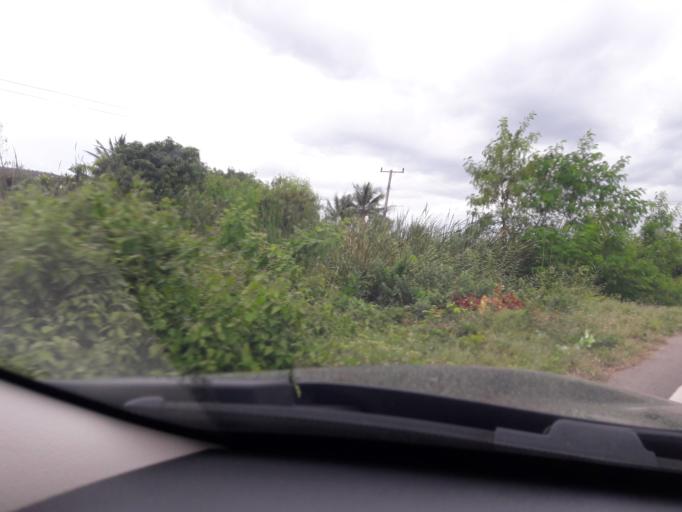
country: TH
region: Ratchaburi
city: Damnoen Saduak
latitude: 13.6032
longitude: 99.9417
